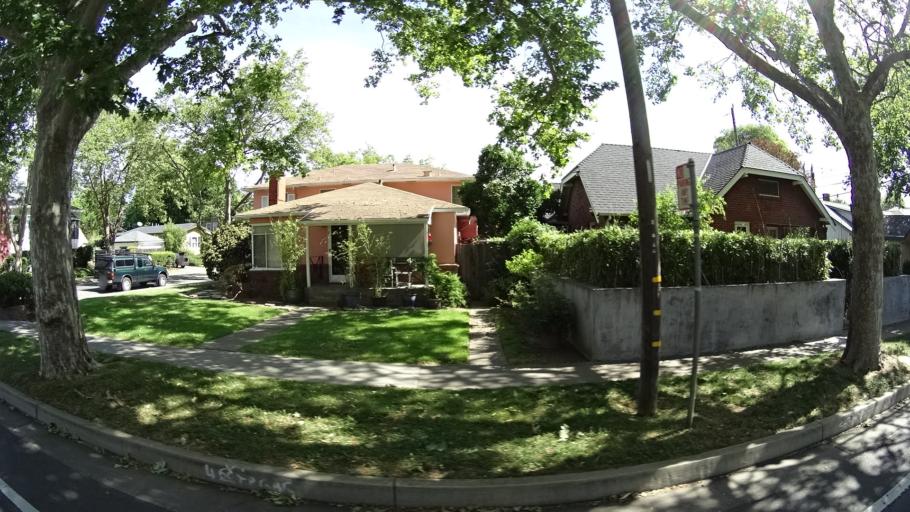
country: US
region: California
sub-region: Sacramento County
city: Sacramento
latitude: 38.5719
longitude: -121.4527
